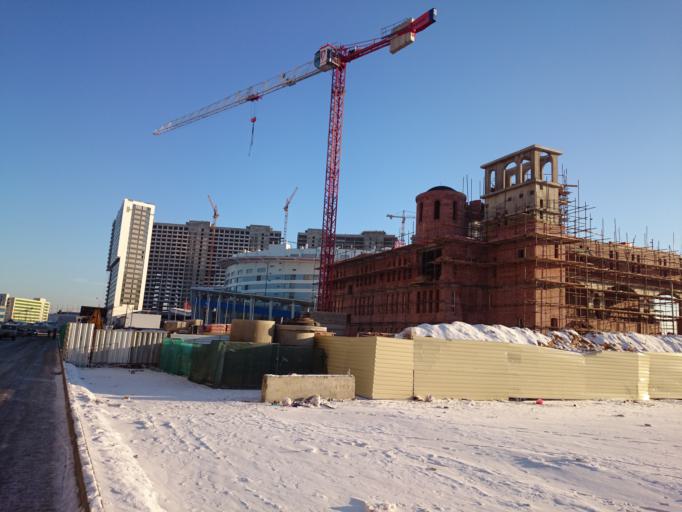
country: RU
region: Moscow
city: Sokol
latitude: 55.7882
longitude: 37.5364
